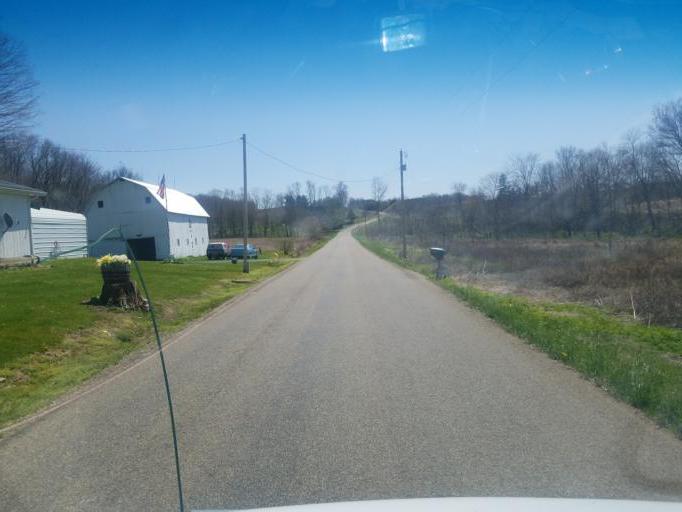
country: US
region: Ohio
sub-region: Knox County
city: Oak Hill
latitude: 40.3732
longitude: -82.3105
